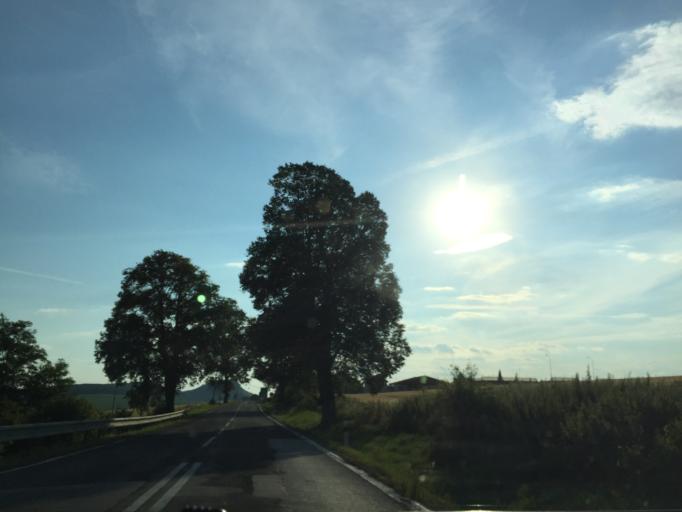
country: SK
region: Presovsky
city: Spisske Podhradie
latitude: 49.0071
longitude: 20.8169
